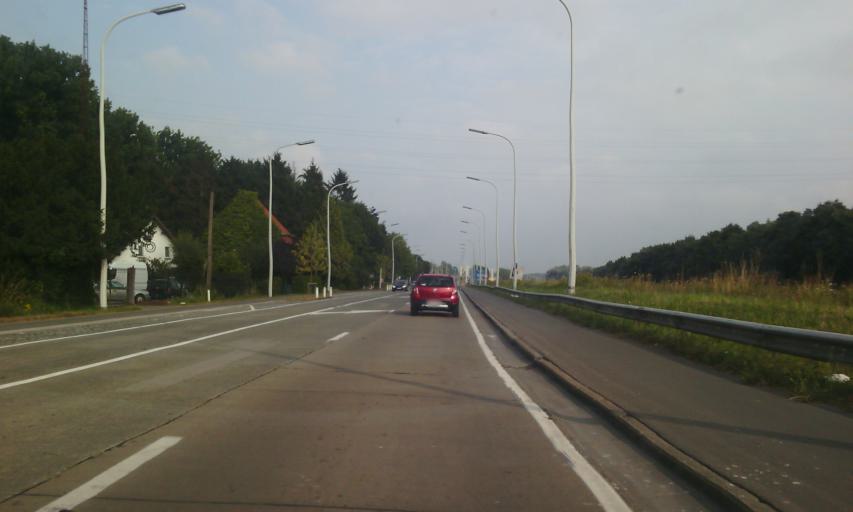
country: BE
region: Flanders
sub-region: Provincie Oost-Vlaanderen
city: Lovendegem
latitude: 51.0915
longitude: 3.6484
